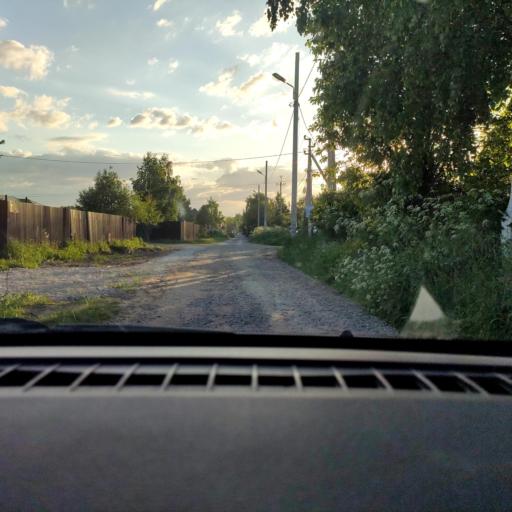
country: RU
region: Perm
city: Polazna
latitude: 58.1289
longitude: 56.4021
